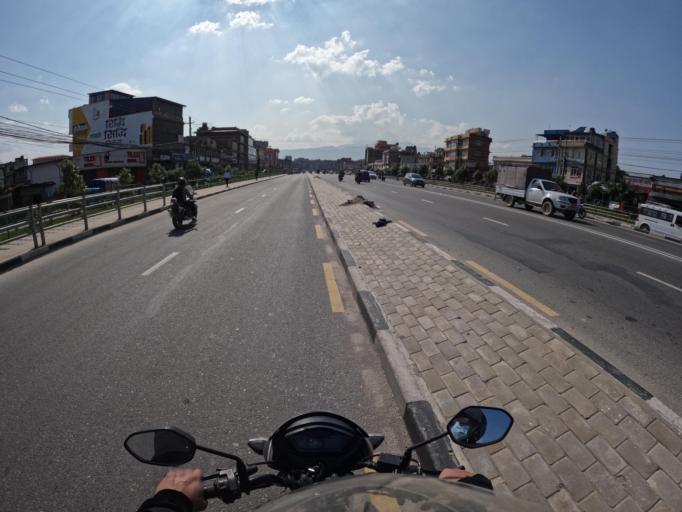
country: NP
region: Central Region
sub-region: Bagmati Zone
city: Patan
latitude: 27.6698
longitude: 85.3375
